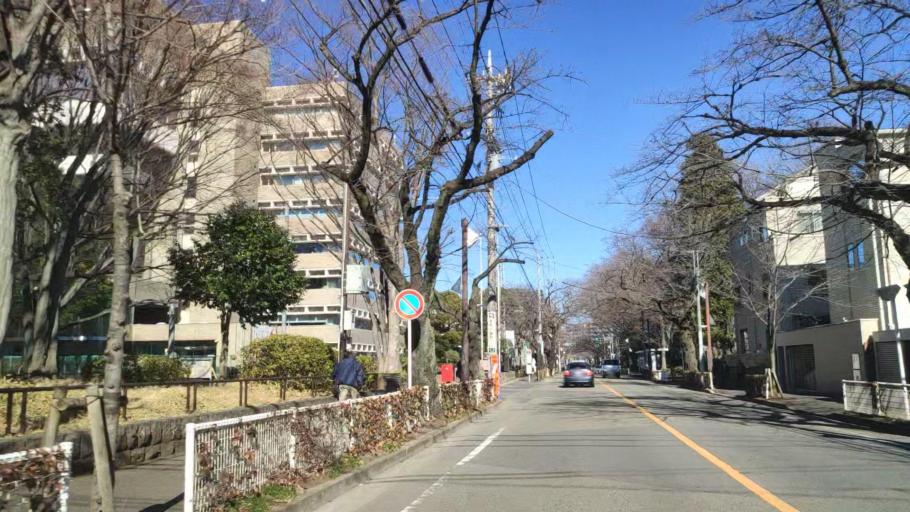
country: JP
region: Tokyo
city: Musashino
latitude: 35.7169
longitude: 139.5662
